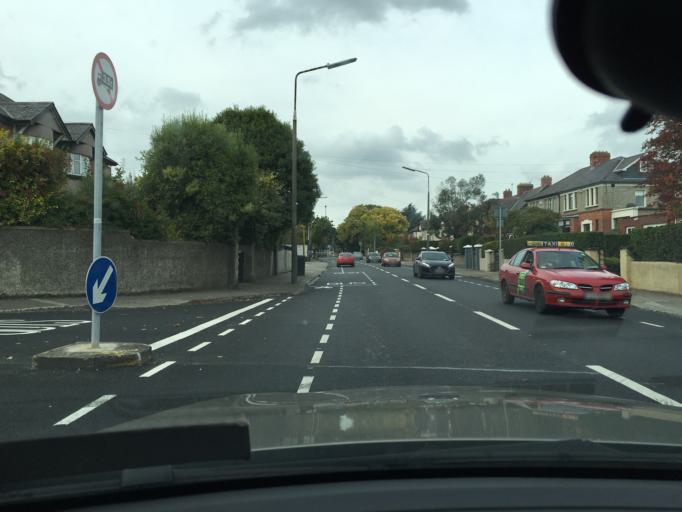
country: IE
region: Leinster
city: Cabra
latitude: 53.3601
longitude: -6.2944
